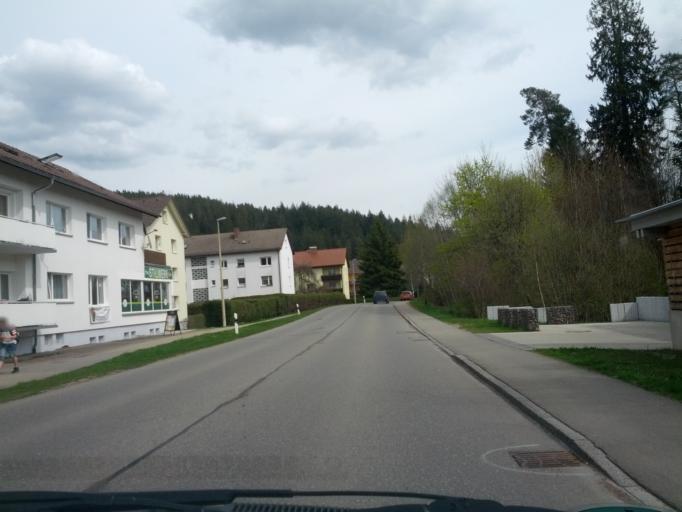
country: DE
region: Baden-Wuerttemberg
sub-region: Freiburg Region
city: Titisee-Neustadt
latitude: 47.9232
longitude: 8.1968
